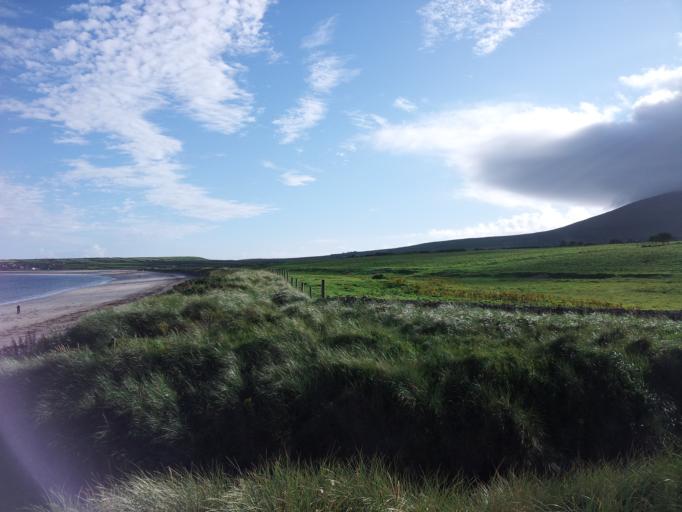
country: IE
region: Munster
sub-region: Ciarrai
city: Dingle
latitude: 52.1271
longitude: -10.3742
